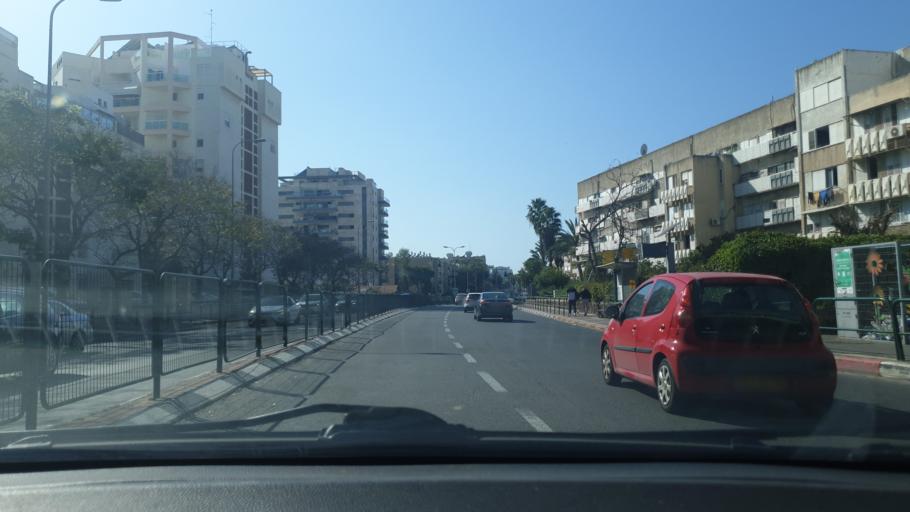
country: IL
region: Tel Aviv
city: Azor
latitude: 32.0451
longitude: 34.8093
